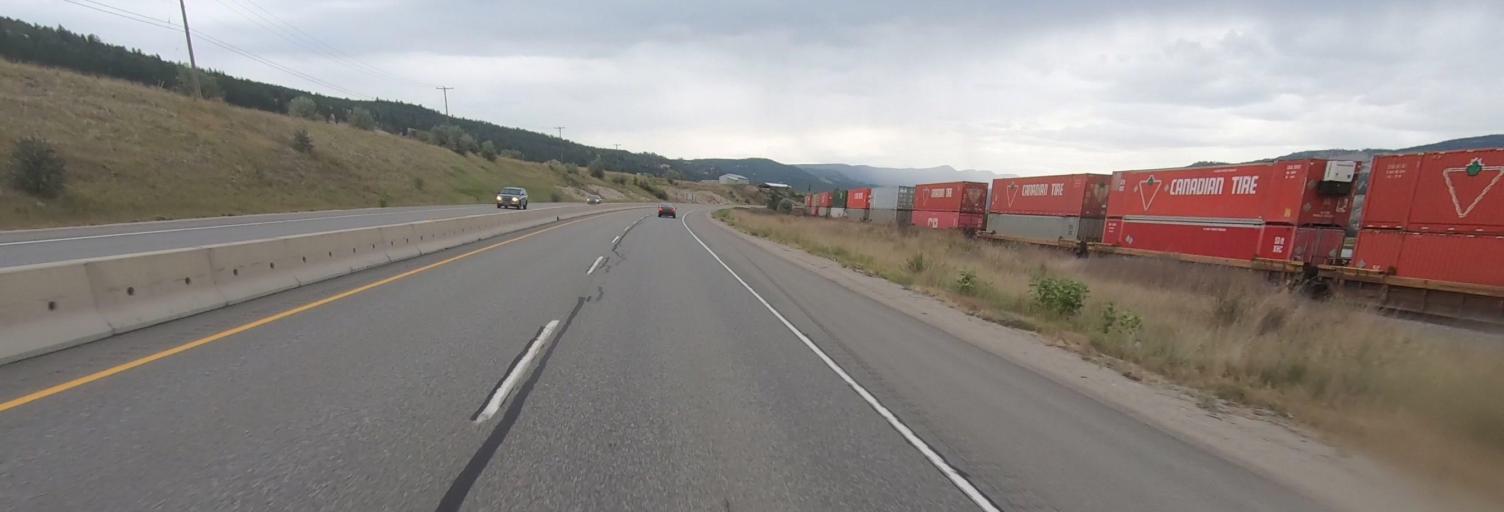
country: CA
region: British Columbia
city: Chase
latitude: 50.6767
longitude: -119.8316
